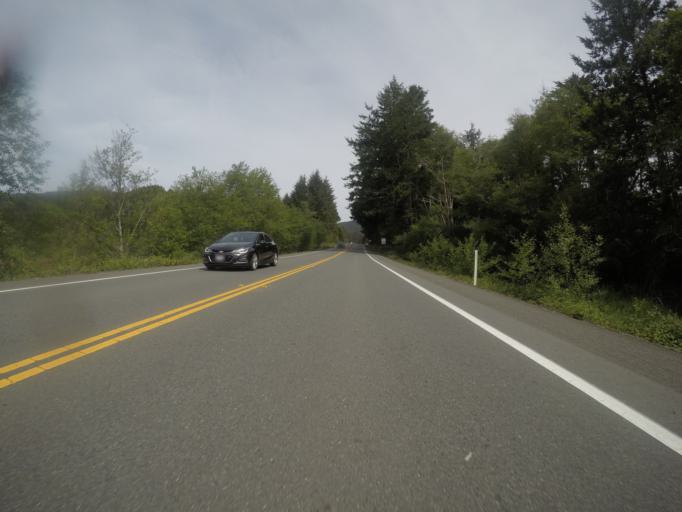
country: US
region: California
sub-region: Del Norte County
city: Bertsch-Oceanview
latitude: 41.5709
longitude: -124.0705
